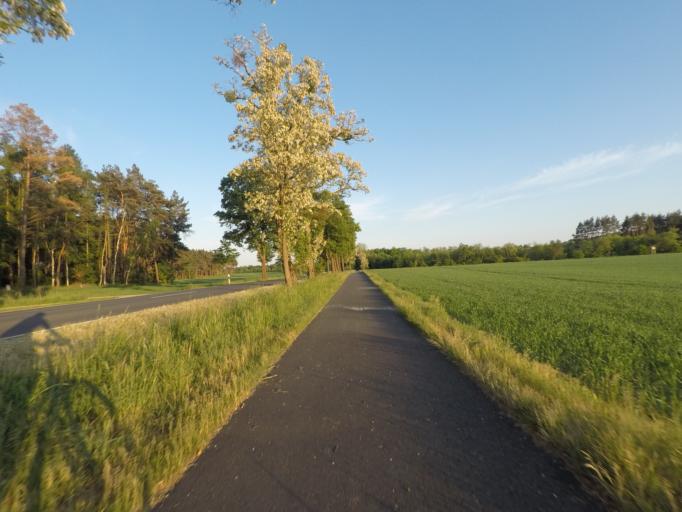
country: DE
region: Brandenburg
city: Marienwerder
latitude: 52.8688
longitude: 13.6427
